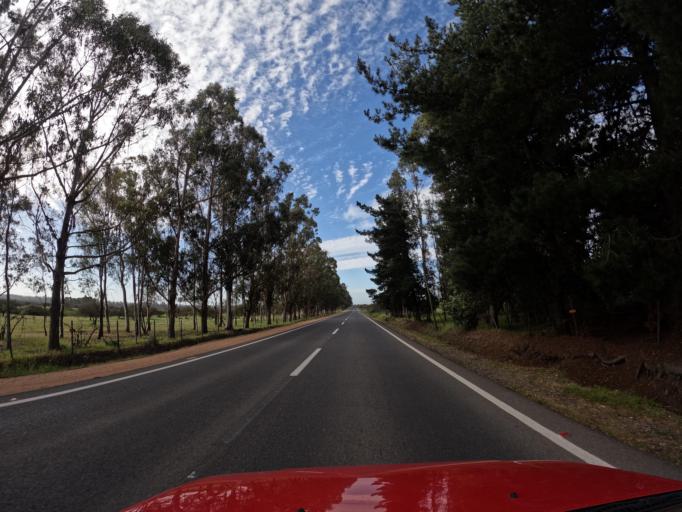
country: CL
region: O'Higgins
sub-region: Provincia de Colchagua
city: Santa Cruz
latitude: -34.1749
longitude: -71.7319
